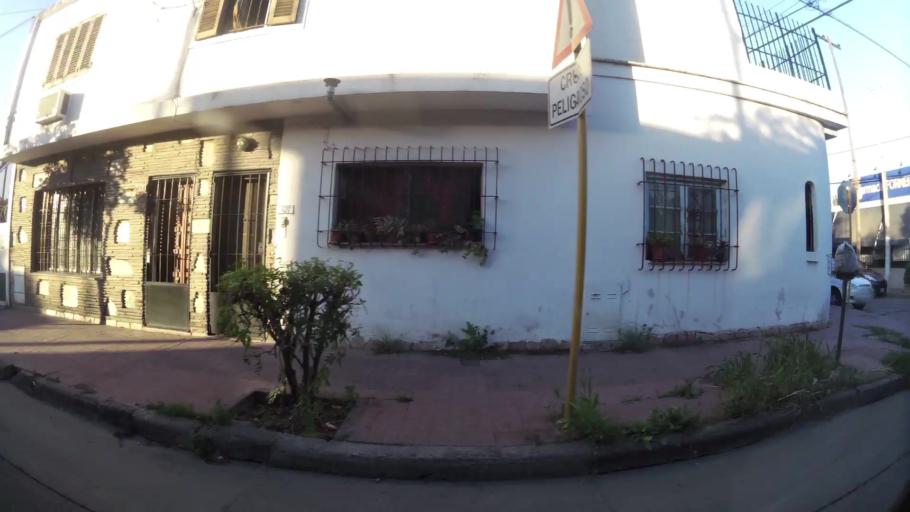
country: AR
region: Cordoba
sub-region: Departamento de Capital
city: Cordoba
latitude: -31.3857
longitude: -64.2117
